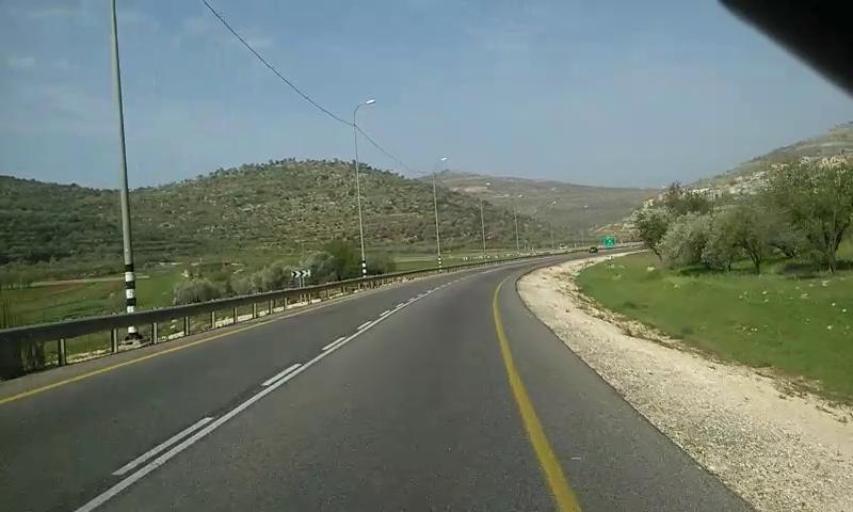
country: PS
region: West Bank
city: Al Lubban ash Sharqiyah
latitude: 32.0666
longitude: 35.2466
